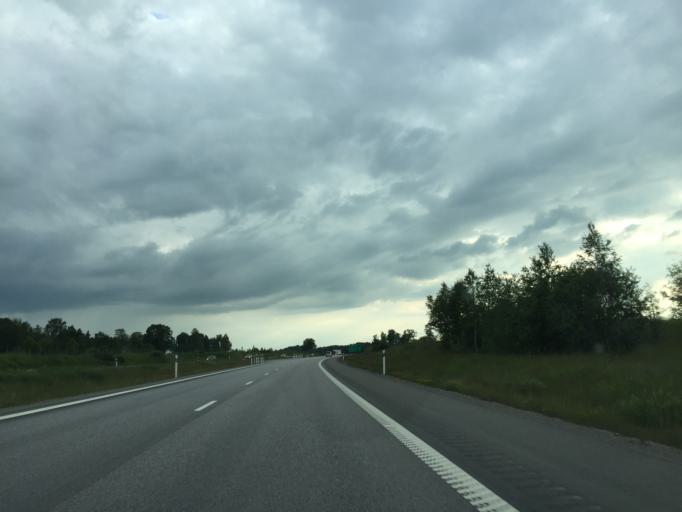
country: SE
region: OErebro
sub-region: Lindesbergs Kommun
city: Fellingsbro
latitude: 59.3333
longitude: 15.5285
